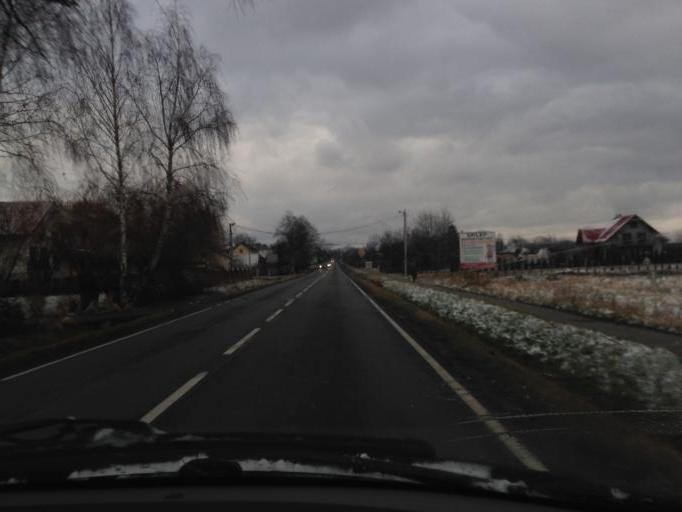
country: PL
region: Lesser Poland Voivodeship
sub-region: Powiat brzeski
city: Czchow
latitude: 49.8535
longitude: 20.6943
